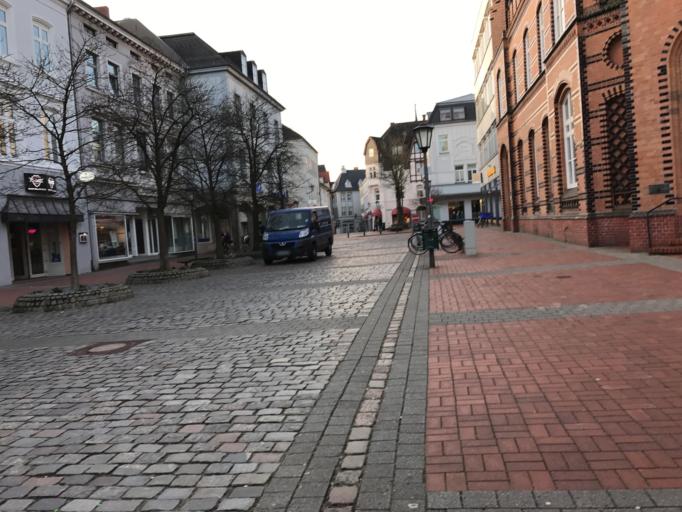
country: DE
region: Schleswig-Holstein
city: Rendsburg
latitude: 54.3037
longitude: 9.6668
